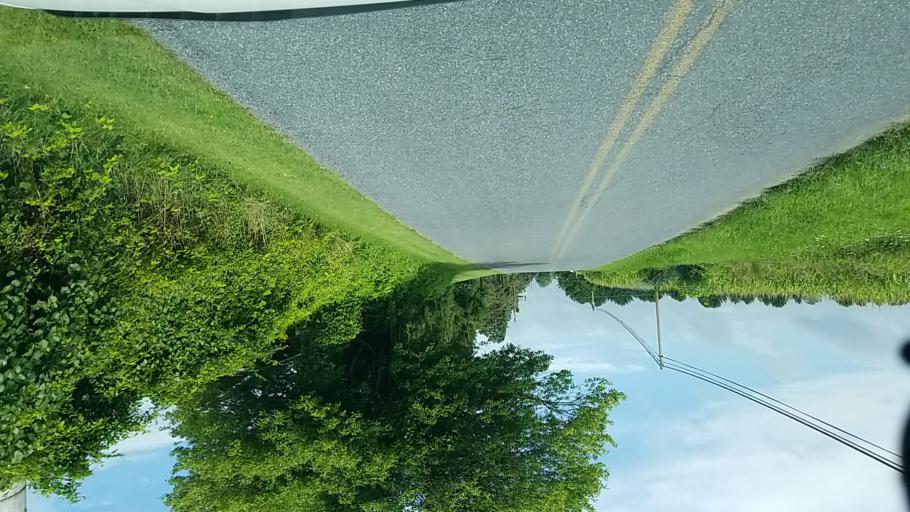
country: US
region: Pennsylvania
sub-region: Dauphin County
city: Millersburg
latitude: 40.5155
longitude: -76.9282
